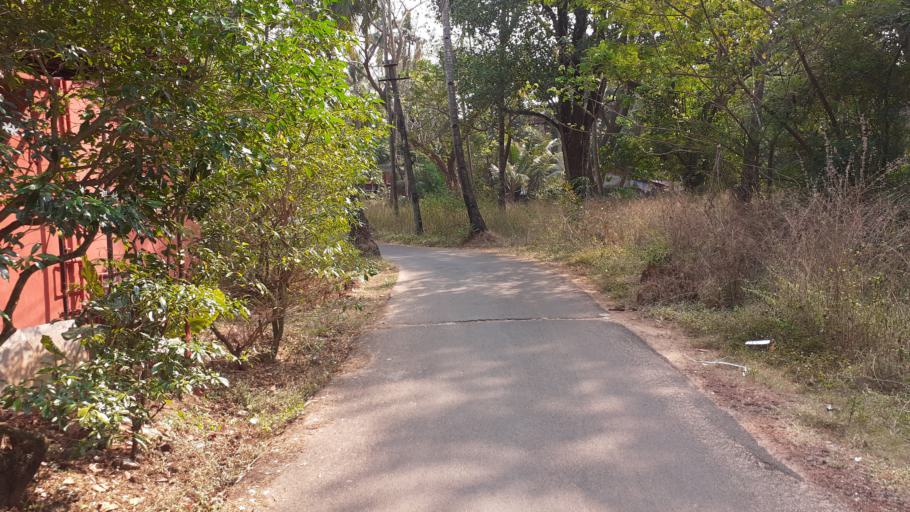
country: IN
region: Goa
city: Calangute
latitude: 15.5672
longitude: 73.7623
